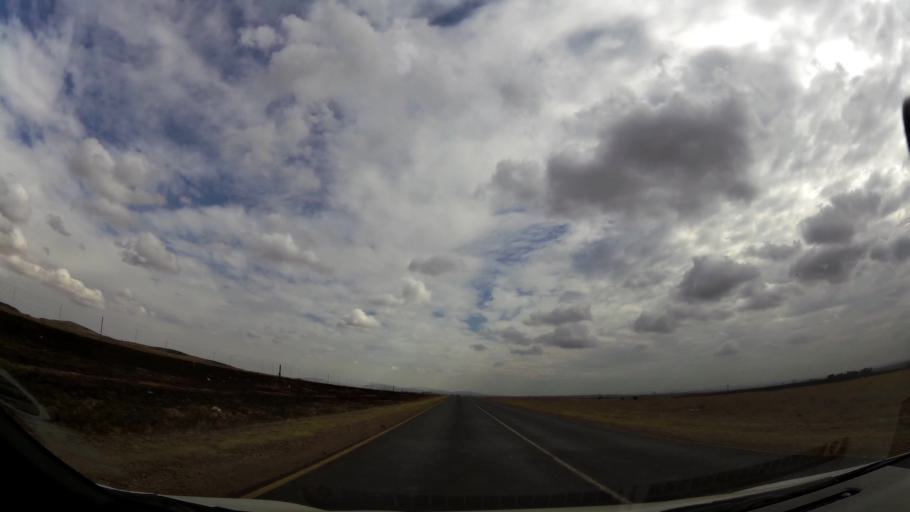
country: ZA
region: Gauteng
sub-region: Sedibeng District Municipality
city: Heidelberg
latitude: -26.4364
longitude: 28.2164
